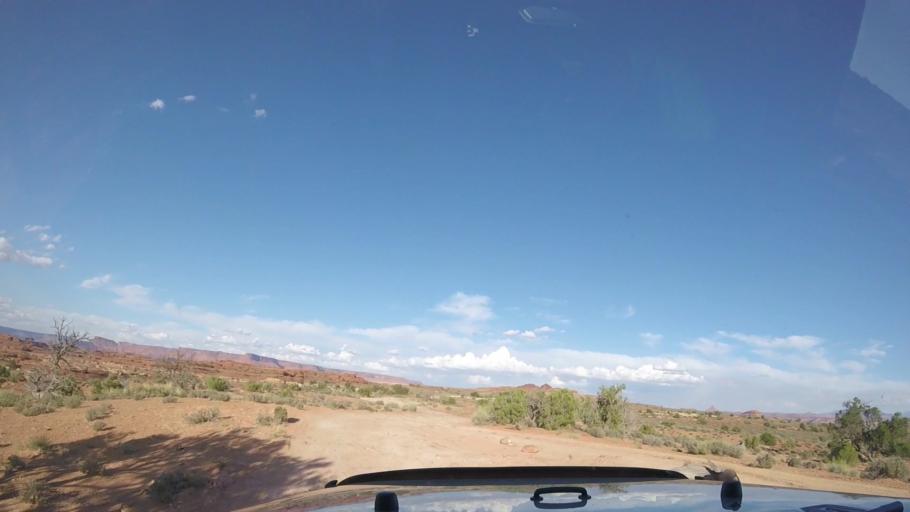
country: US
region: Utah
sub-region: Grand County
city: Moab
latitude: 38.2158
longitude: -109.7995
